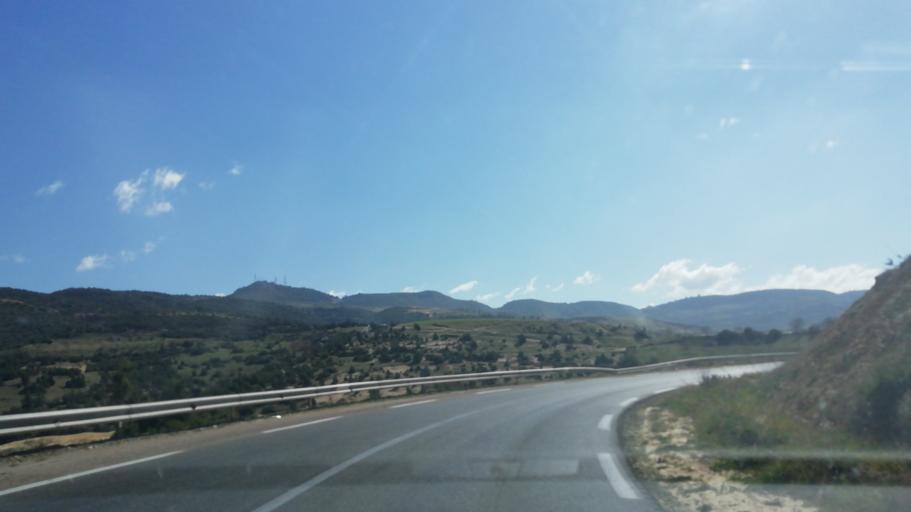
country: DZ
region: Mascara
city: Mascara
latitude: 35.4929
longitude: 0.1372
